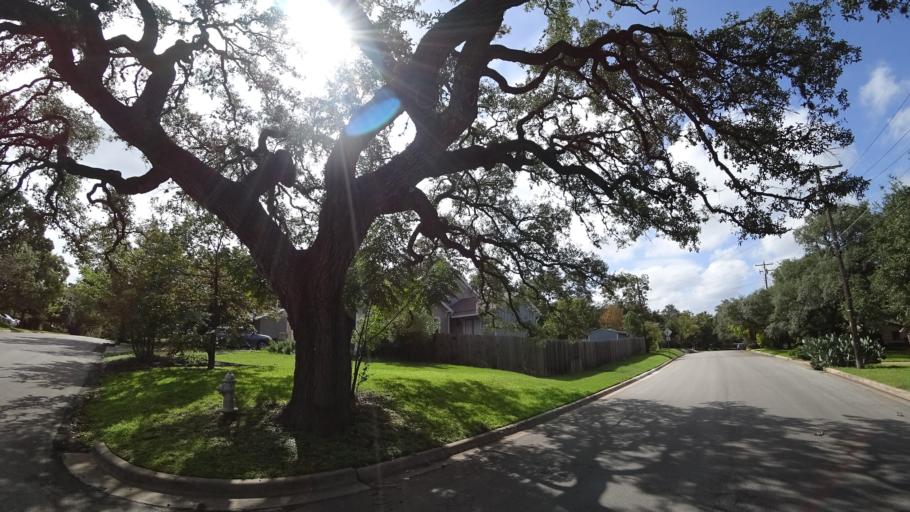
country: US
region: Texas
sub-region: Travis County
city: West Lake Hills
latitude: 30.3470
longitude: -97.7431
